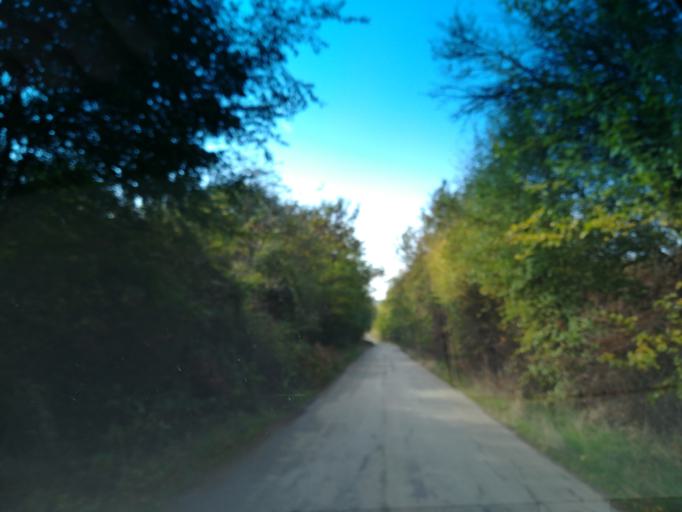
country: BG
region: Stara Zagora
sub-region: Obshtina Nikolaevo
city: Elkhovo
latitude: 42.3297
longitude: 25.4022
